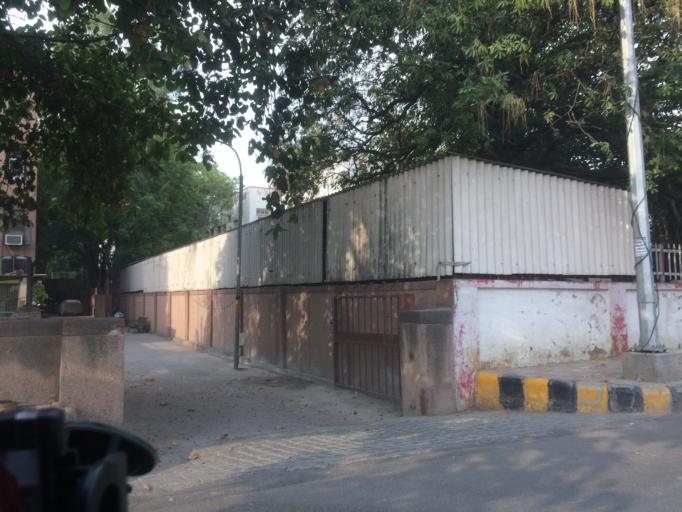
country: IN
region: NCT
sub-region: New Delhi
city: New Delhi
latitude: 28.5760
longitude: 77.1999
